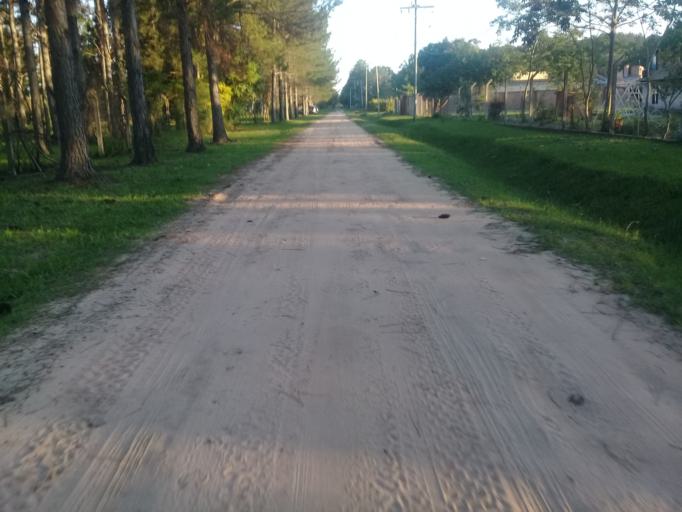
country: AR
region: Corrientes
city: San Luis del Palmar
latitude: -27.4668
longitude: -58.6680
